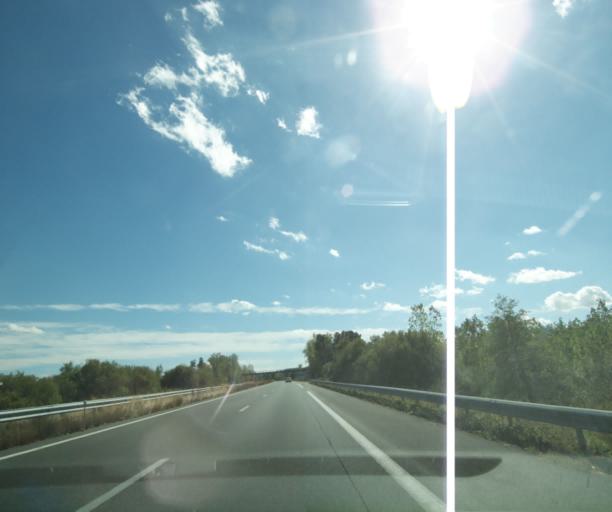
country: FR
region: Aquitaine
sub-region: Departement du Lot-et-Garonne
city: Damazan
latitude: 44.2962
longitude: 0.2612
